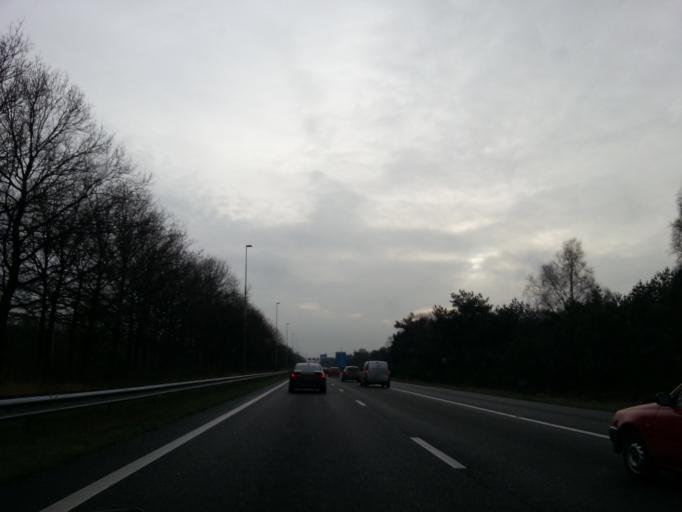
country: NL
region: Gelderland
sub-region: Gemeente Rozendaal
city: Rozendaal
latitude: 52.0551
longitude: 5.9386
